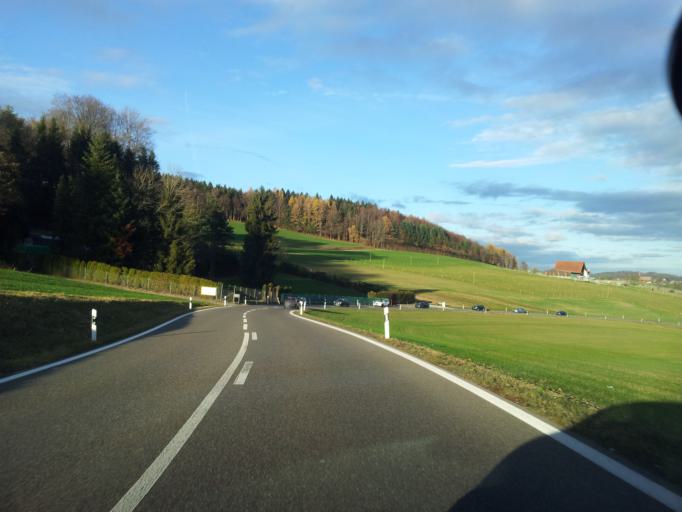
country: CH
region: Aargau
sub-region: Bezirk Bremgarten
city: Unterlunkhofen
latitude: 47.3434
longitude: 8.4066
